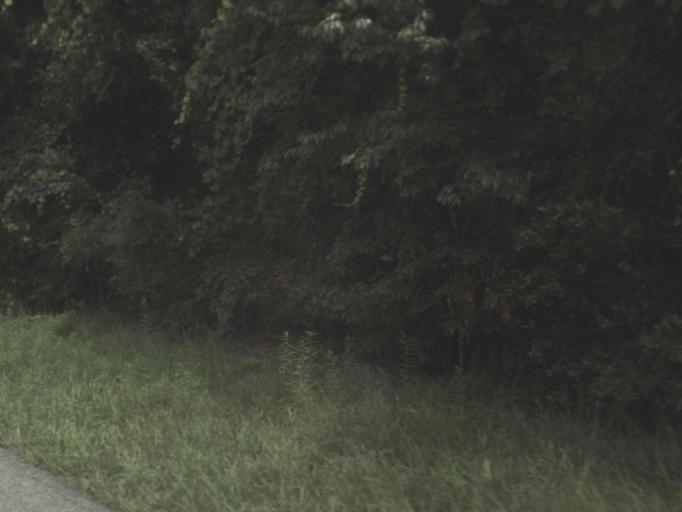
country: US
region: Florida
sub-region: Levy County
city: Chiefland
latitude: 29.4268
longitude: -82.8889
